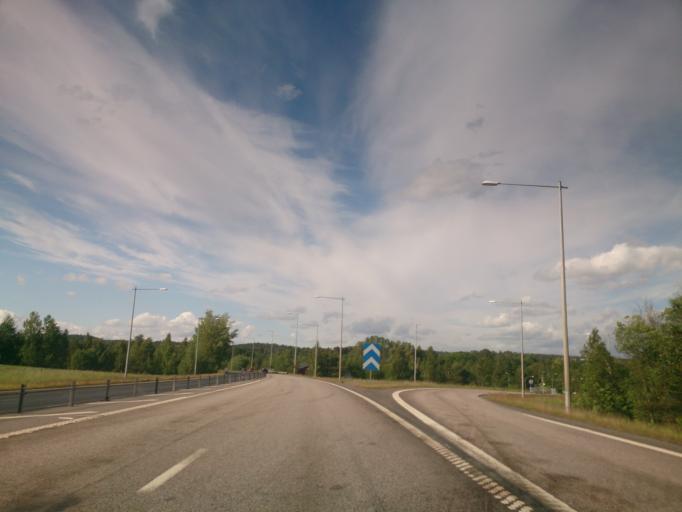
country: SE
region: OEstergoetland
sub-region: Norrkopings Kommun
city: Jursla
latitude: 58.6549
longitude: 16.1702
